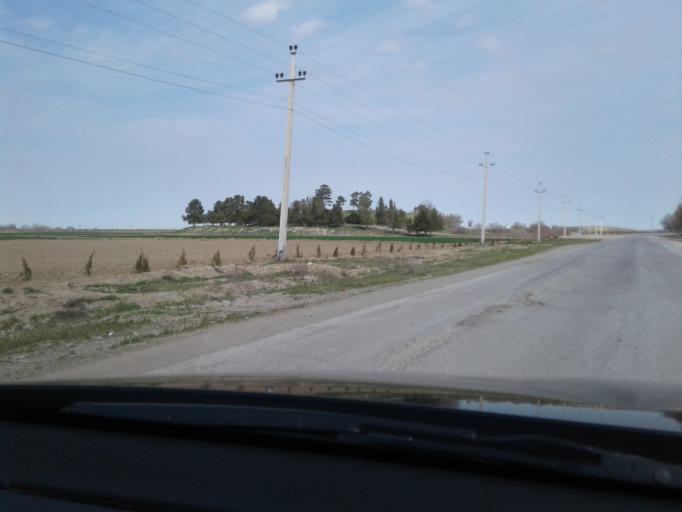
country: TM
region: Ahal
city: Abadan
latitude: 38.1217
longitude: 58.3450
